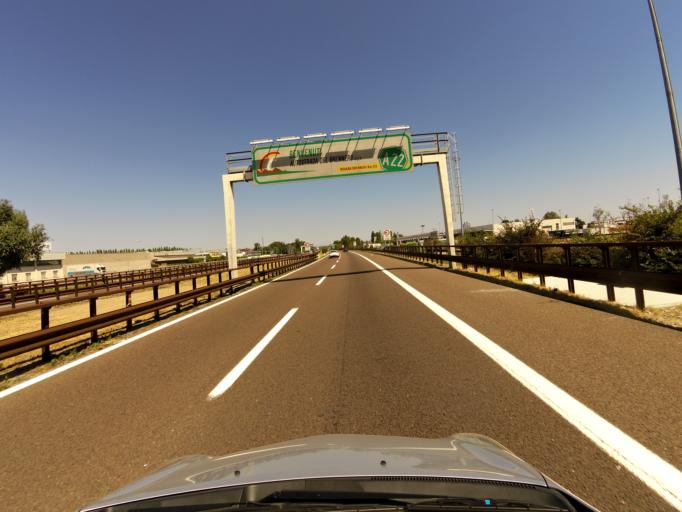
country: IT
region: Emilia-Romagna
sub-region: Provincia di Modena
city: Campogalliano
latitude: 44.6784
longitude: 10.8485
